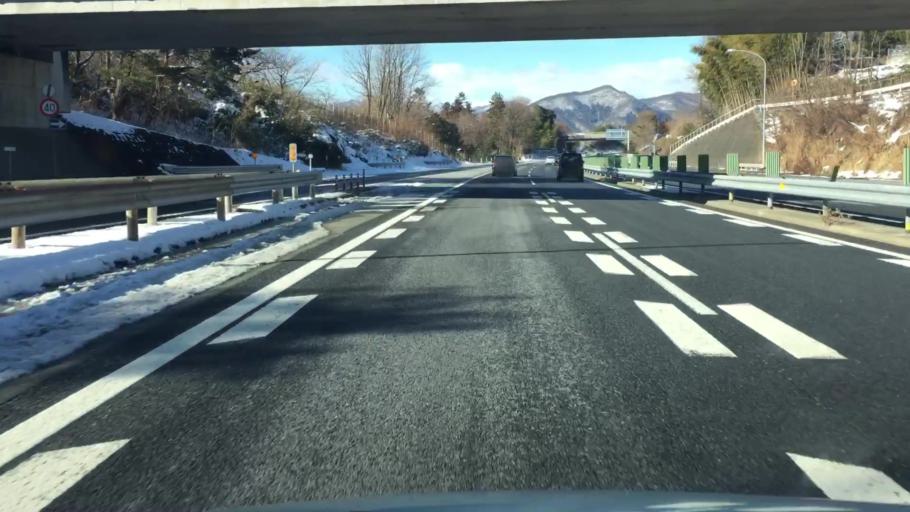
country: JP
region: Gunma
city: Numata
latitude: 36.6766
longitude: 139.0171
